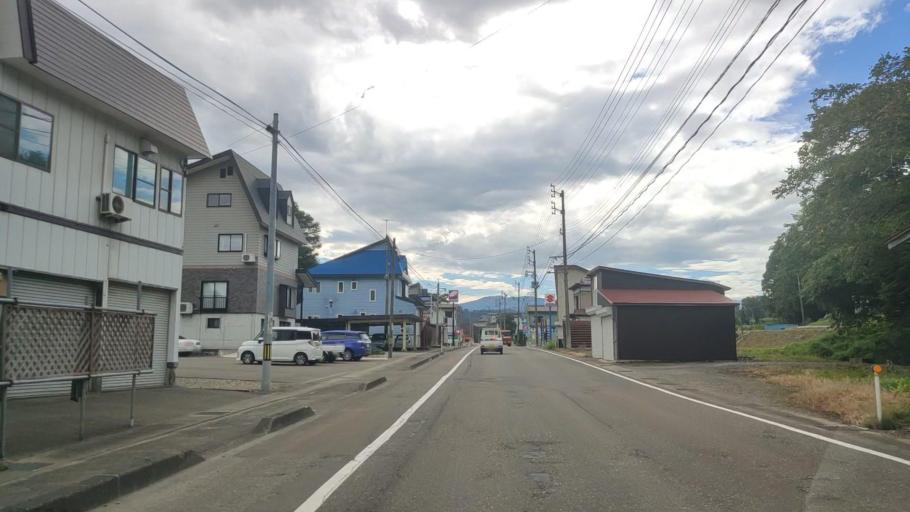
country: JP
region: Niigata
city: Arai
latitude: 36.9915
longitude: 138.2701
